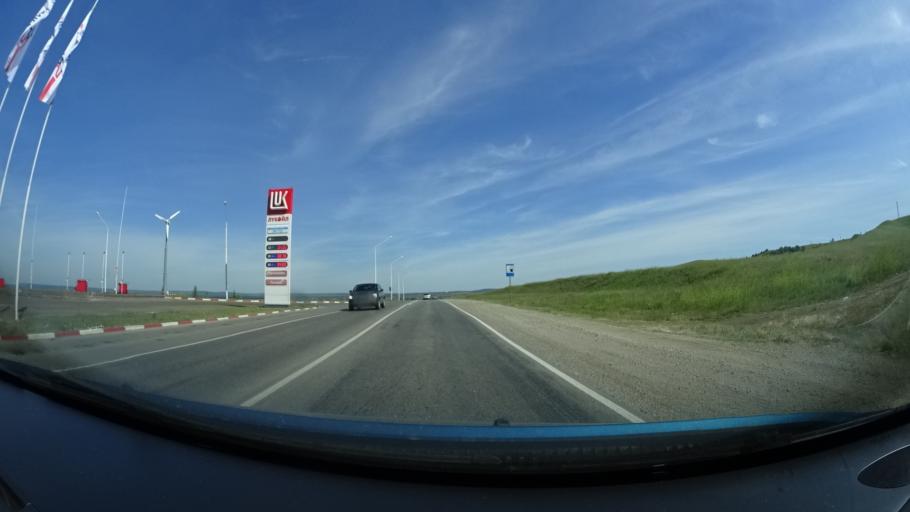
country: RU
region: Bashkortostan
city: Blagoveshchensk
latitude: 55.1765
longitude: 55.8537
